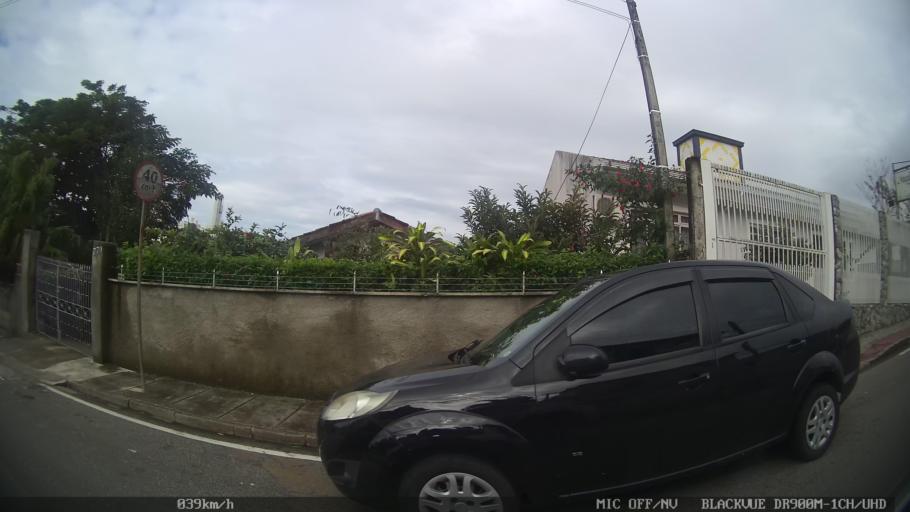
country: BR
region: Santa Catarina
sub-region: Sao Jose
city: Campinas
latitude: -27.5443
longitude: -48.6262
